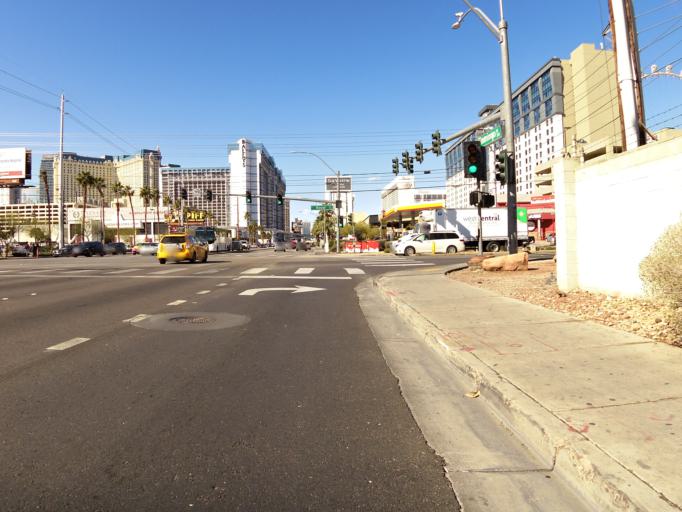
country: US
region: Nevada
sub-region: Clark County
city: Paradise
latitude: 36.1147
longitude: -115.1637
